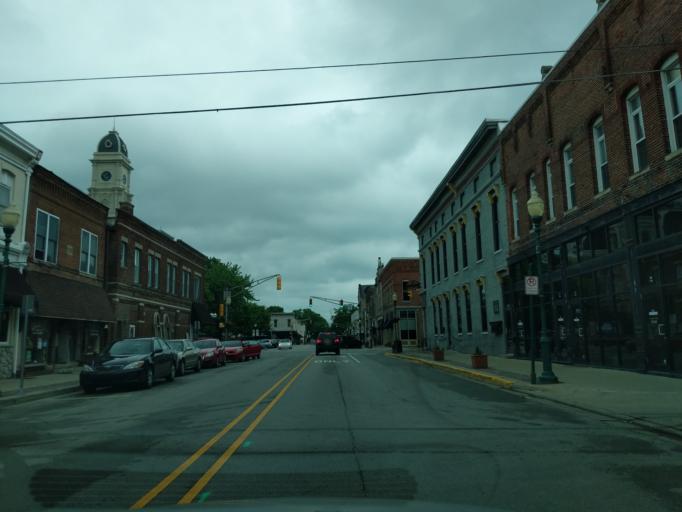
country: US
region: Indiana
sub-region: Hamilton County
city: Noblesville
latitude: 40.0450
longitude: -86.0135
